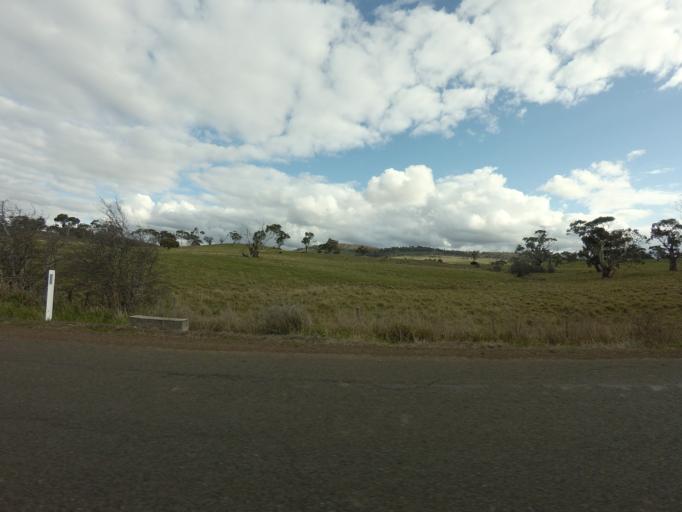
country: AU
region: Tasmania
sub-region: Northern Midlands
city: Evandale
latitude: -41.8874
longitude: 147.3166
